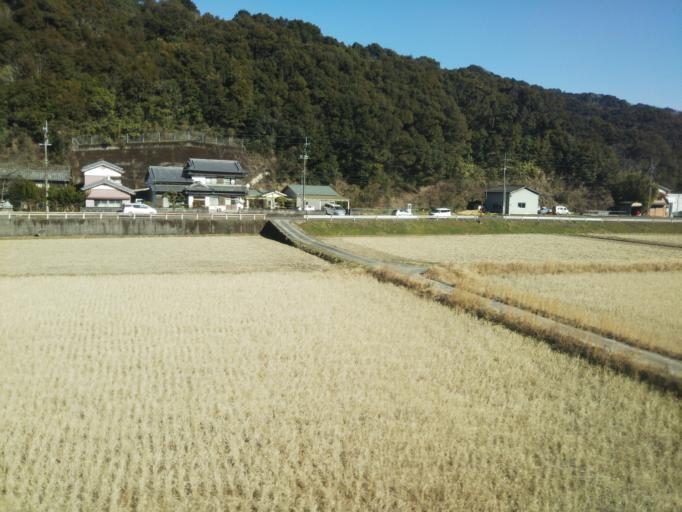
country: JP
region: Kochi
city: Nakamura
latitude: 33.1007
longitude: 133.0993
